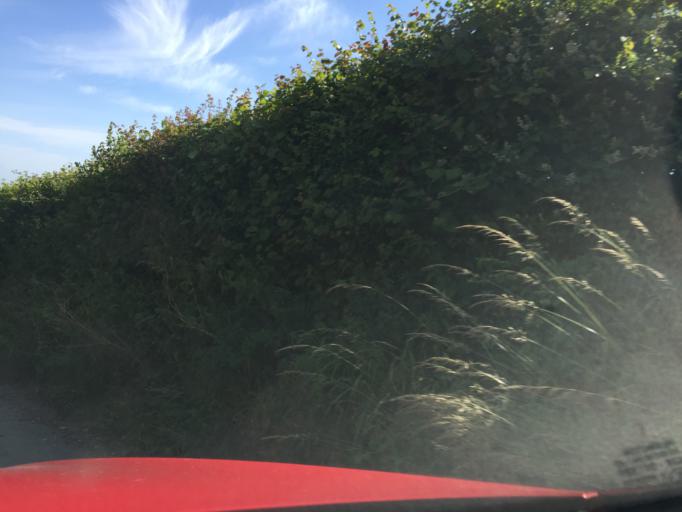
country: GB
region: England
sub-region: Gloucestershire
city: Stonehouse
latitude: 51.7825
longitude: -2.2602
